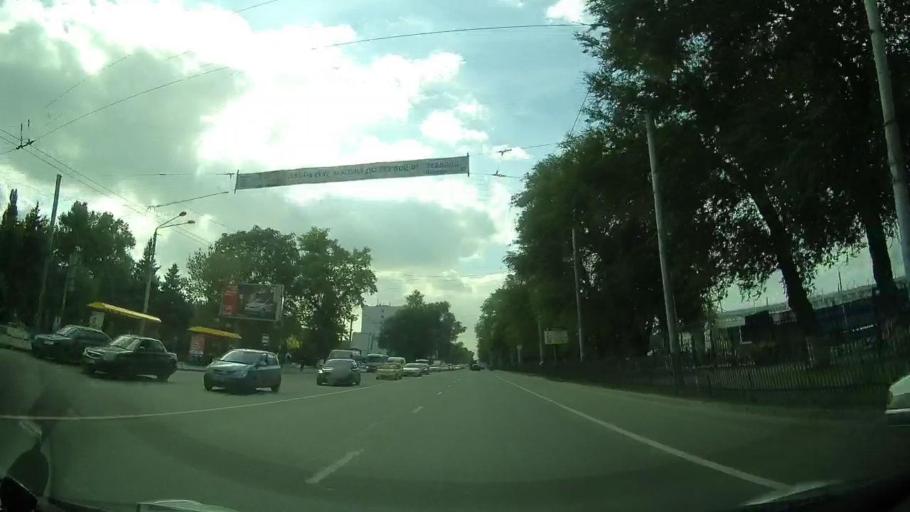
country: RU
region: Rostov
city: Imeni Chkalova
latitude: 47.2586
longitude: 39.8034
